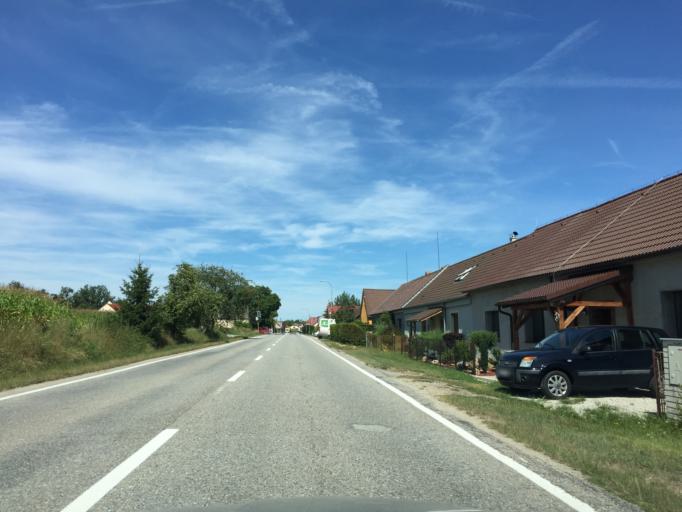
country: CZ
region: Jihocesky
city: Sevetin
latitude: 49.0859
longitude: 14.5424
